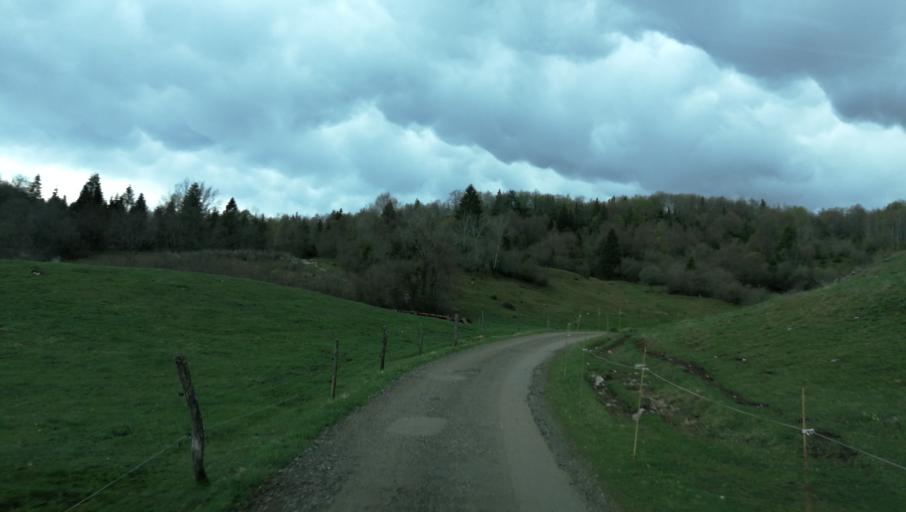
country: FR
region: Franche-Comte
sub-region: Departement du Jura
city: Lavans-les-Saint-Claude
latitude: 46.3192
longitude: 5.8100
